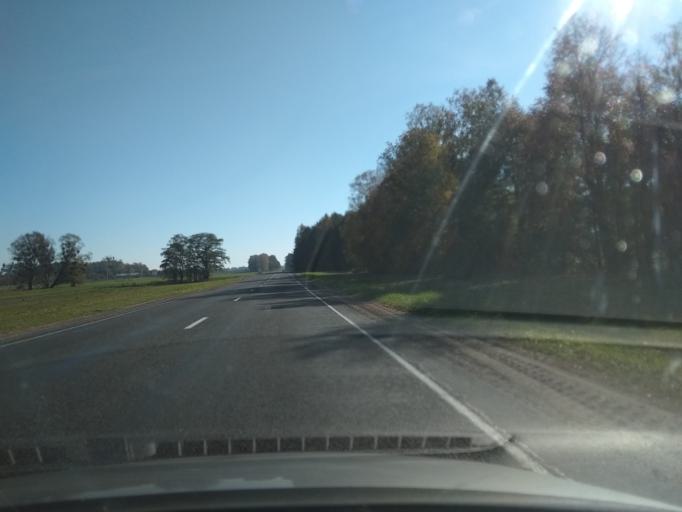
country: BY
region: Brest
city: Malaryta
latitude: 51.9366
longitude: 24.0451
